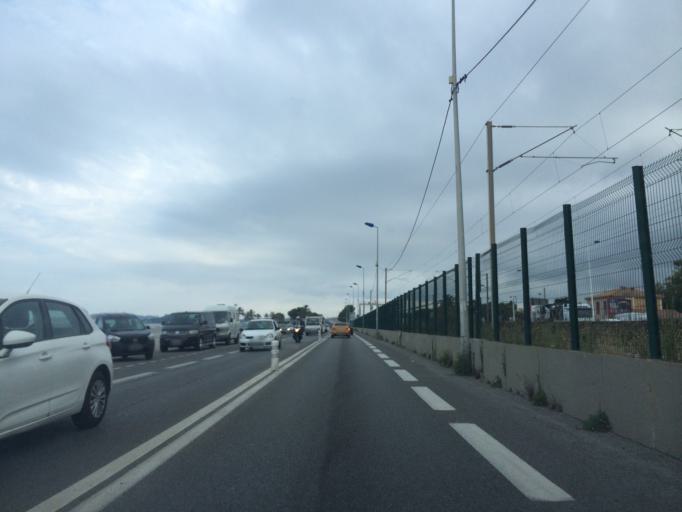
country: FR
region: Provence-Alpes-Cote d'Azur
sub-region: Departement des Alpes-Maritimes
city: Biot
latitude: 43.6144
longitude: 7.1279
